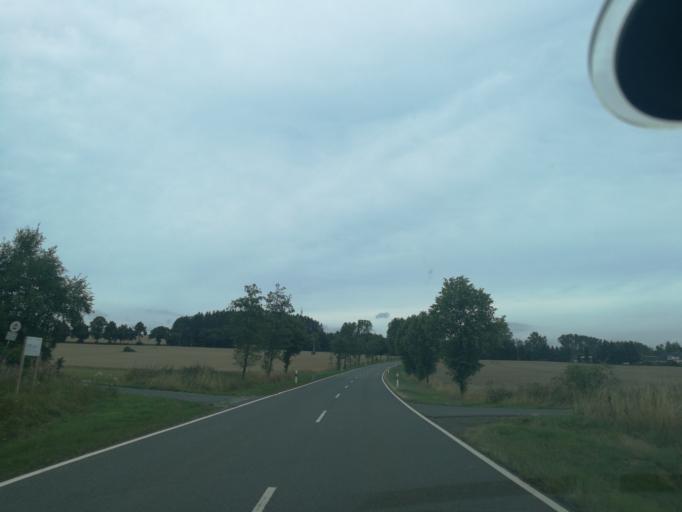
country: DE
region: Bavaria
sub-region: Upper Franconia
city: Regnitzlosau
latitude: 50.3320
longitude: 12.0694
